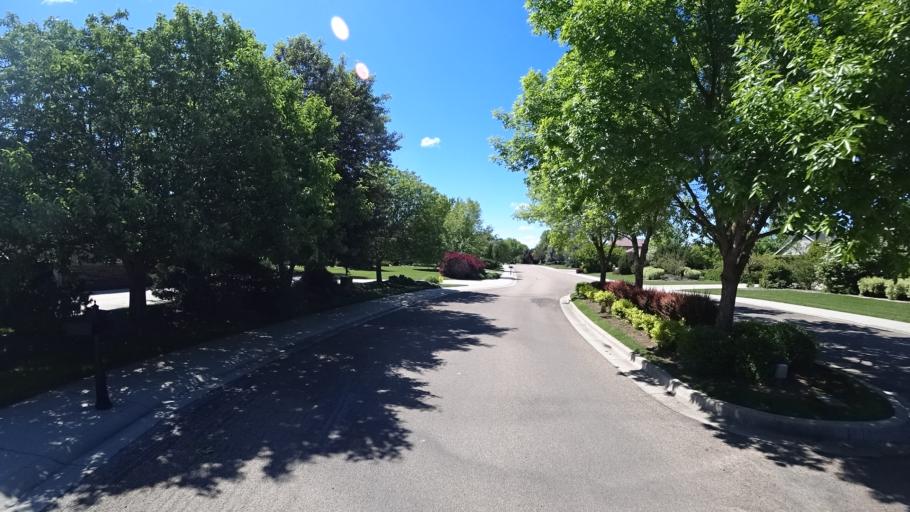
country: US
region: Idaho
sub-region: Ada County
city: Eagle
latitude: 43.6660
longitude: -116.3804
